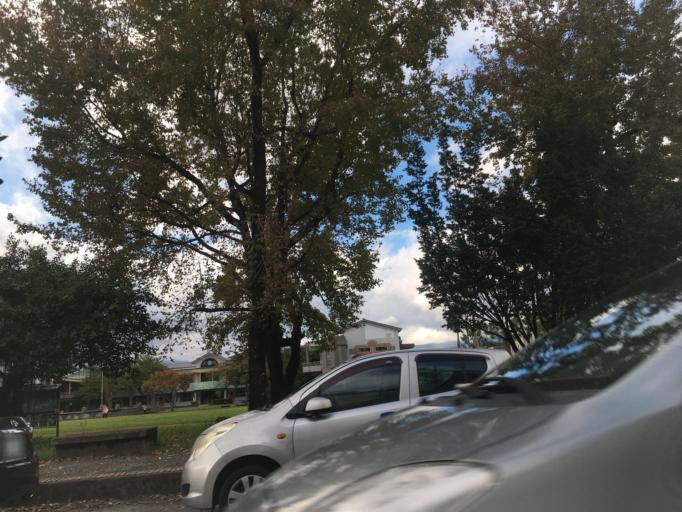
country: TW
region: Taiwan
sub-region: Yilan
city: Yilan
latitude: 24.6925
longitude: 121.7286
